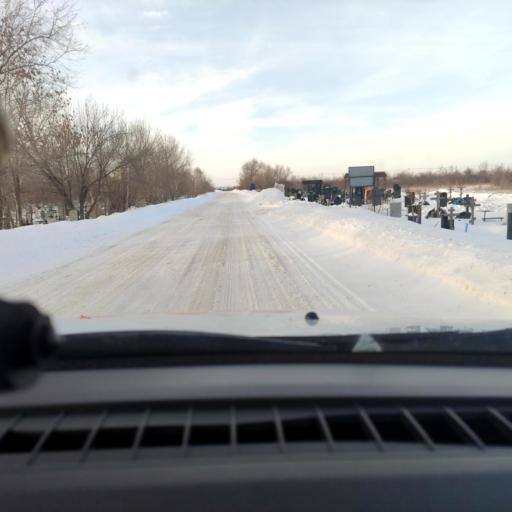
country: RU
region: Samara
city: Chapayevsk
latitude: 52.9903
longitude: 49.7444
